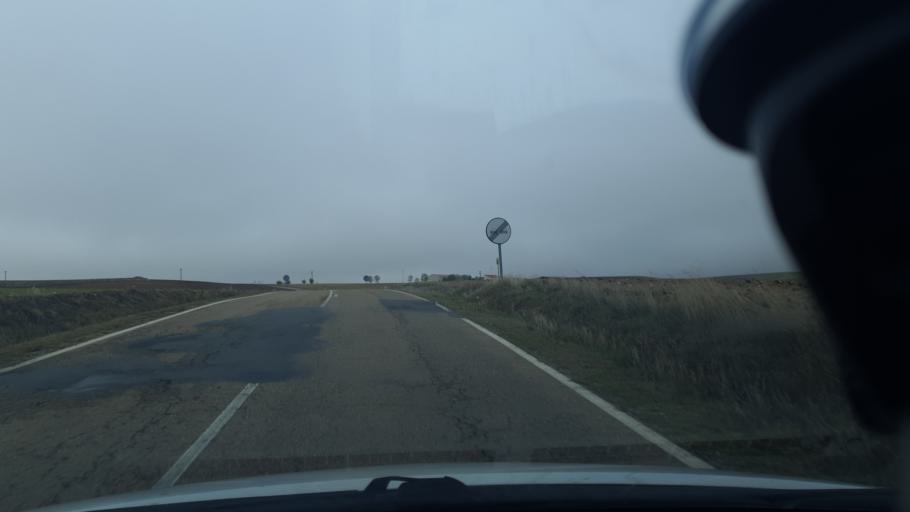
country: ES
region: Castille and Leon
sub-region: Provincia de Segovia
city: Hontanares de Eresma
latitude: 40.9921
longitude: -4.1956
